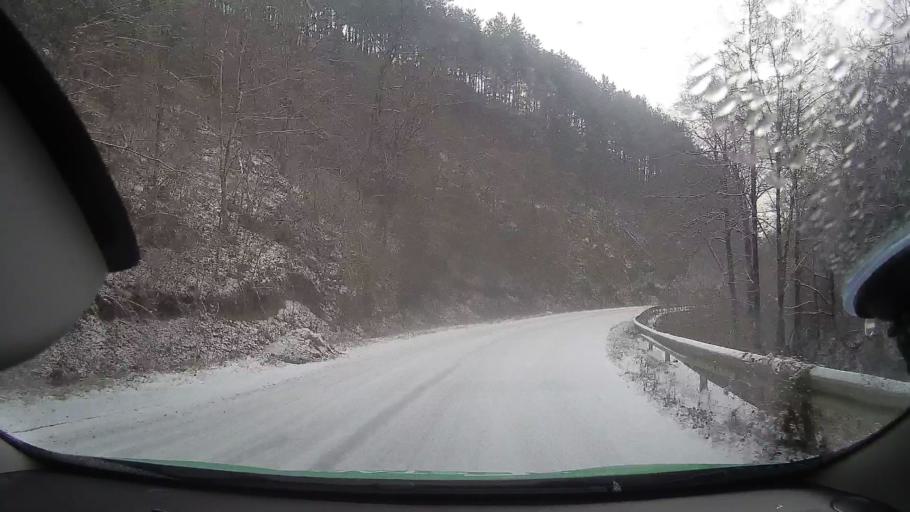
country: RO
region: Alba
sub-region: Comuna Livezile
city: Livezile
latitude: 46.3718
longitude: 23.5874
